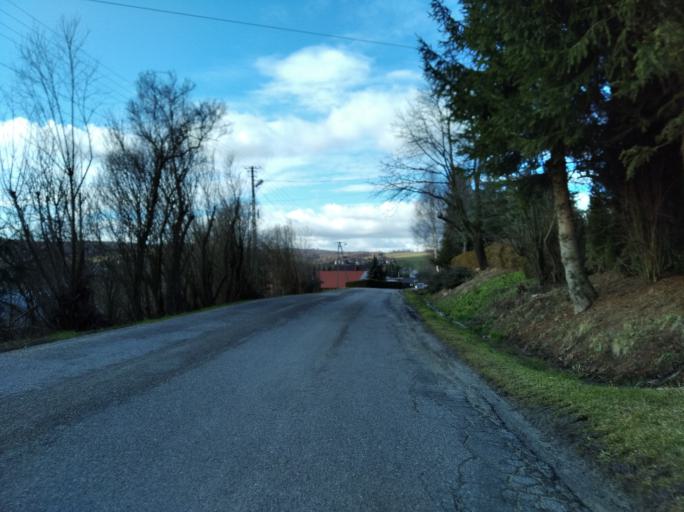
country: PL
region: Subcarpathian Voivodeship
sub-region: Powiat strzyzowski
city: Wisniowa
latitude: 49.9115
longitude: 21.6833
